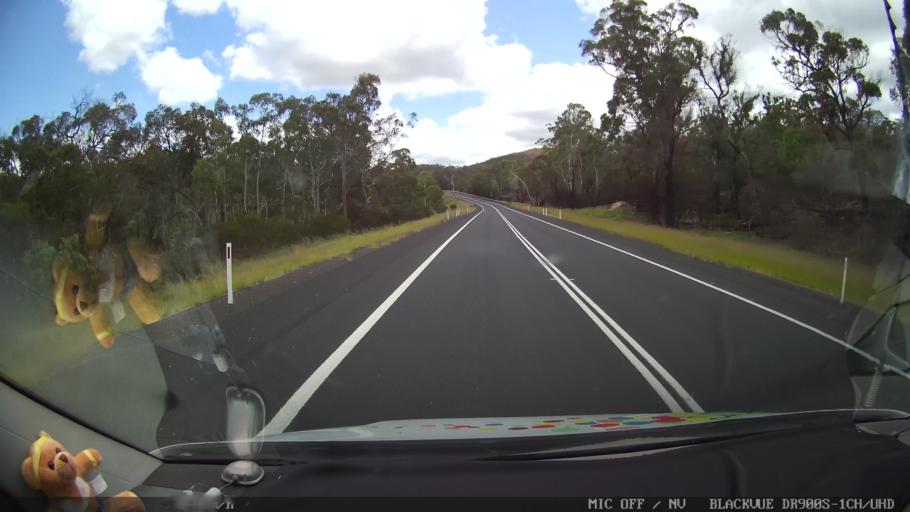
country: AU
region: New South Wales
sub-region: Glen Innes Severn
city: Glen Innes
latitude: -29.3550
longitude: 151.8972
